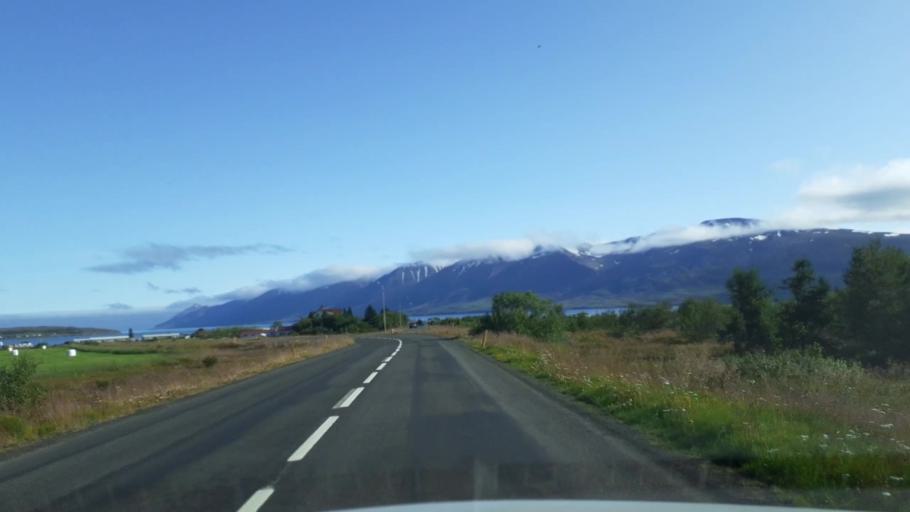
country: IS
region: Northeast
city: Dalvik
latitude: 65.9381
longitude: -18.3539
